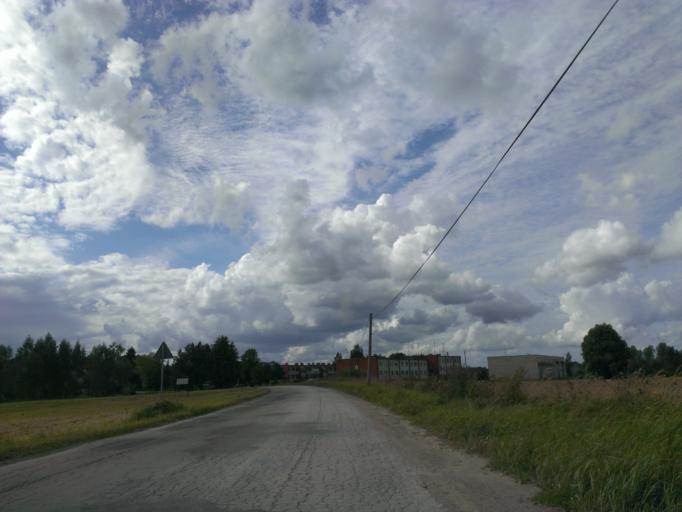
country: LV
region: Skriveri
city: Skriveri
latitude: 56.8458
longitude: 25.1679
